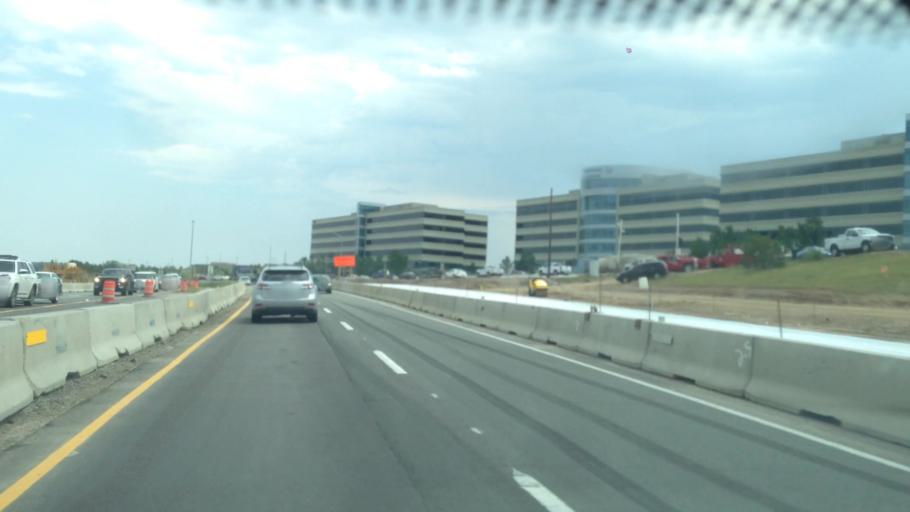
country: US
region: Colorado
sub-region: Douglas County
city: Highlands Ranch
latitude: 39.5594
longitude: -105.0062
